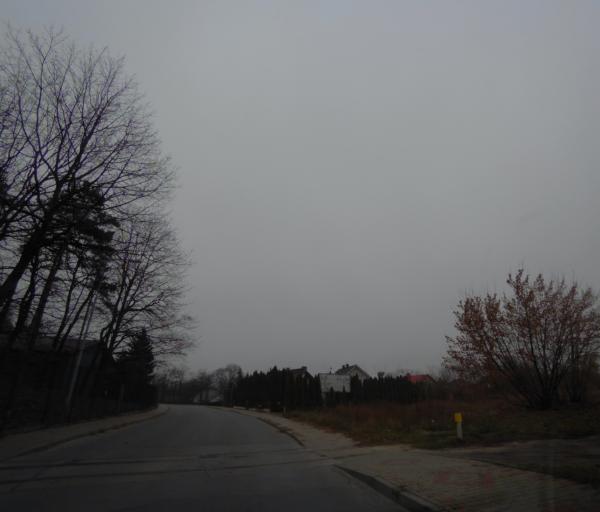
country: PL
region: Subcarpathian Voivodeship
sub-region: Powiat lezajski
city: Lezajsk
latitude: 50.2688
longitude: 22.4177
